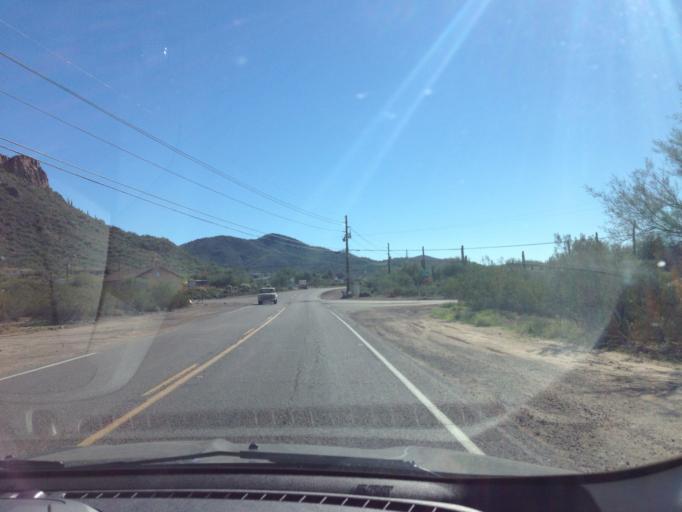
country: US
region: Arizona
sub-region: Maricopa County
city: Anthem
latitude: 33.8723
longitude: -112.0657
